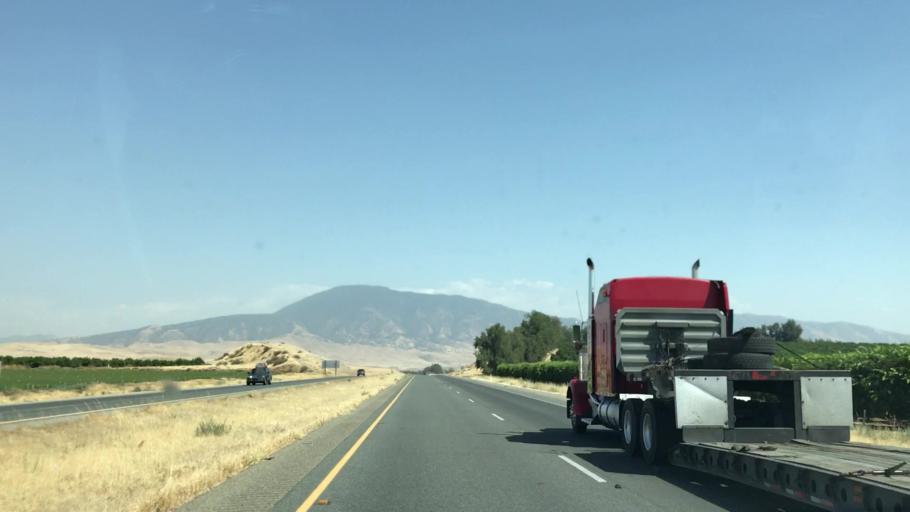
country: US
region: California
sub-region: Kern County
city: Arvin
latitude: 35.3205
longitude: -118.7933
